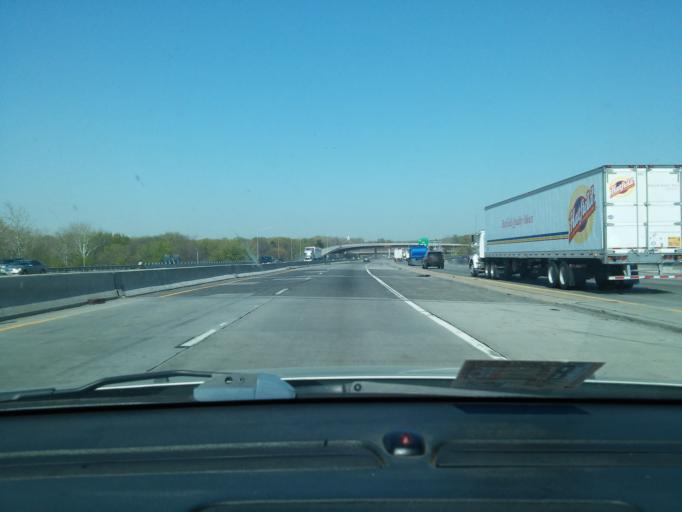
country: US
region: New Jersey
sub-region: Union County
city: Hillside
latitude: 40.7052
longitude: -74.2437
